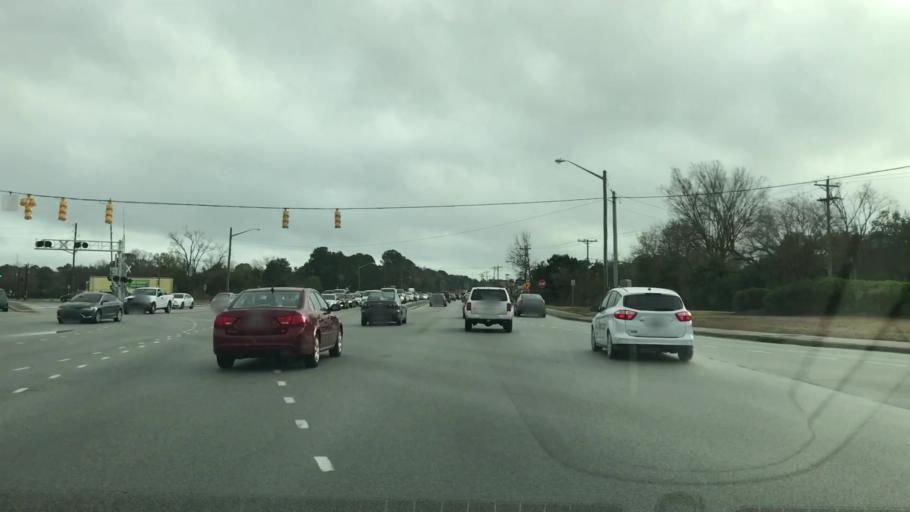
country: US
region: South Carolina
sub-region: Berkeley County
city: Goose Creek
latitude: 32.9962
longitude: -80.0358
